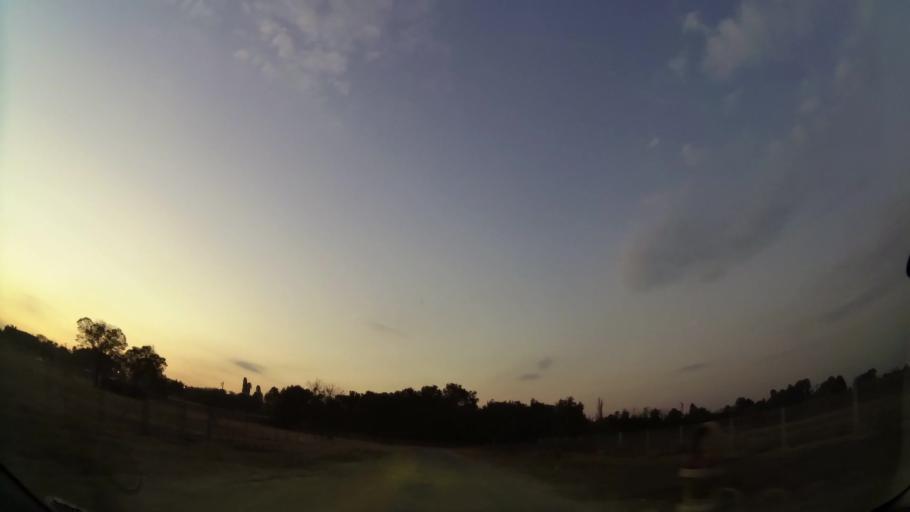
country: ZA
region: Gauteng
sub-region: Ekurhuleni Metropolitan Municipality
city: Benoni
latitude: -26.1142
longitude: 28.3036
